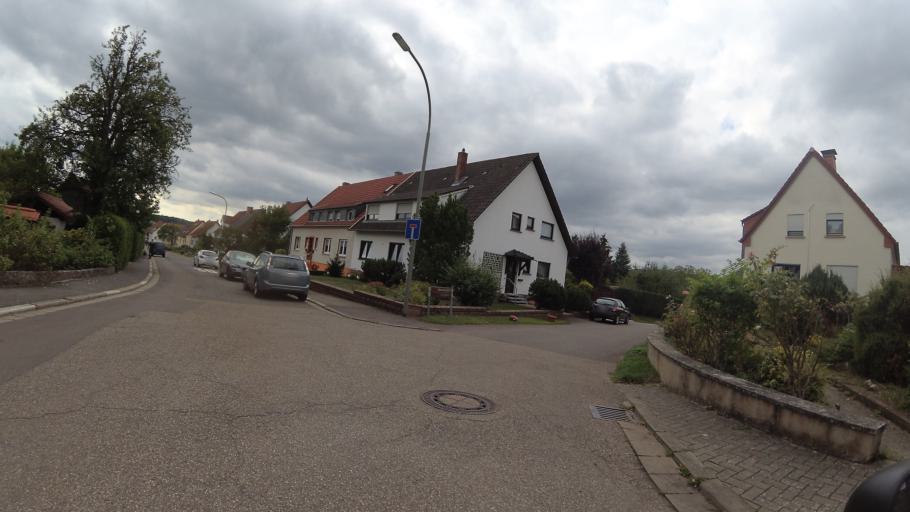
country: DE
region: Saarland
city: Kleinblittersdorf
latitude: 49.1646
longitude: 7.0836
